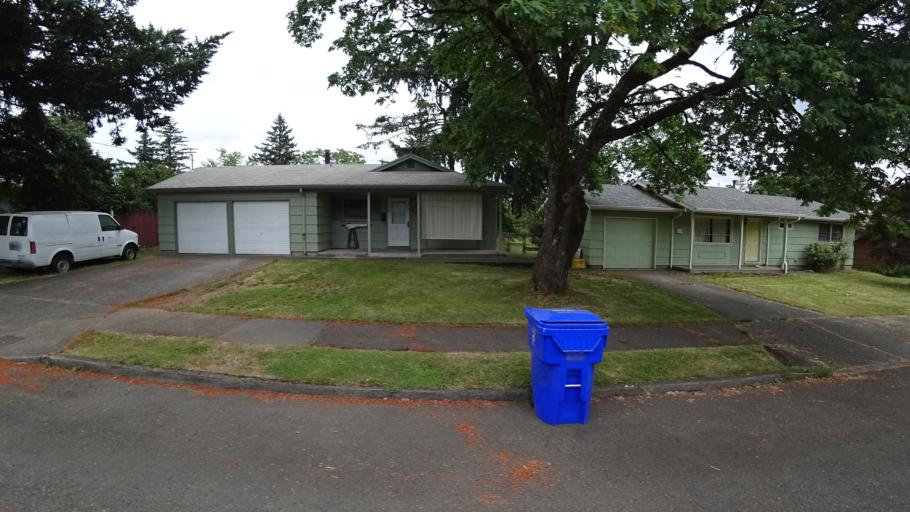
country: US
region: Oregon
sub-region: Multnomah County
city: Lents
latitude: 45.4646
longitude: -122.5835
